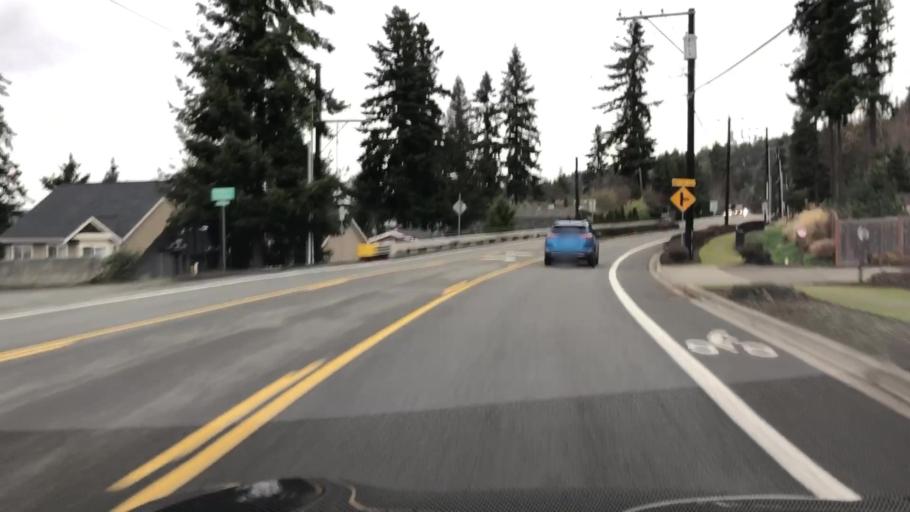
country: US
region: Washington
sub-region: King County
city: Sammamish
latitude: 47.6234
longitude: -122.0702
